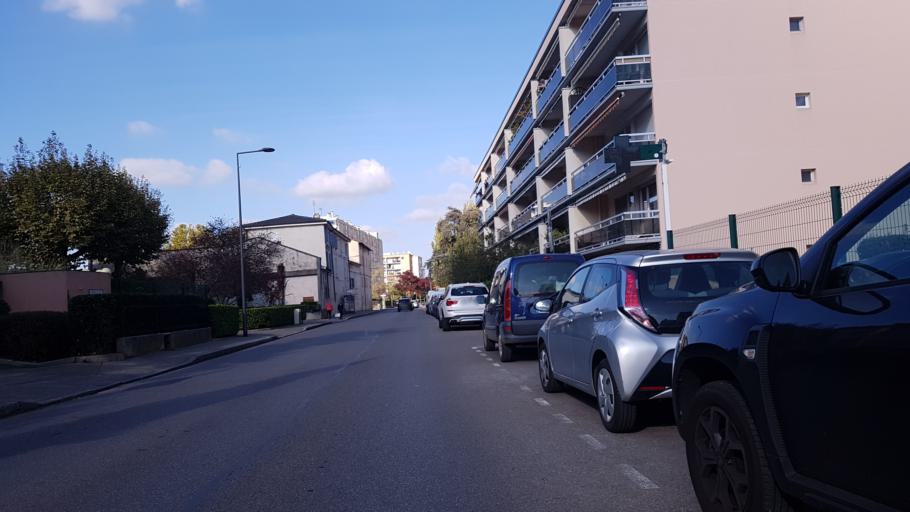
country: FR
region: Rhone-Alpes
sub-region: Departement du Rhone
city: Caluire-et-Cuire
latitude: 45.7852
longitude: 4.8298
